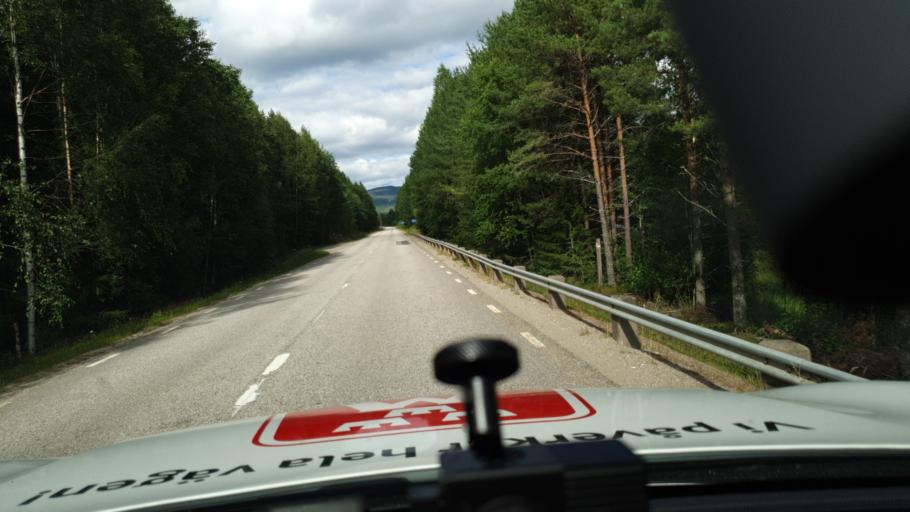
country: NO
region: Hedmark
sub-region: Trysil
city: Innbygda
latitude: 61.0351
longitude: 12.5862
